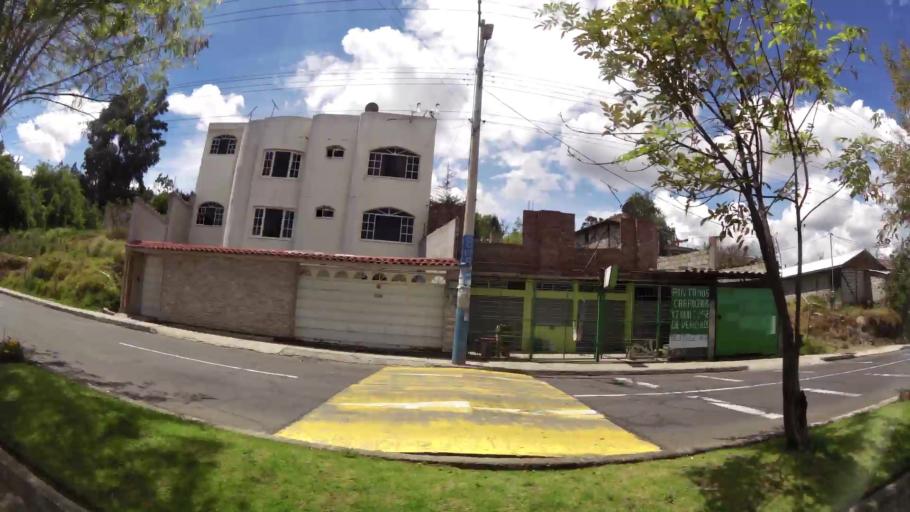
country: EC
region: Tungurahua
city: Ambato
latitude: -1.2780
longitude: -78.6405
